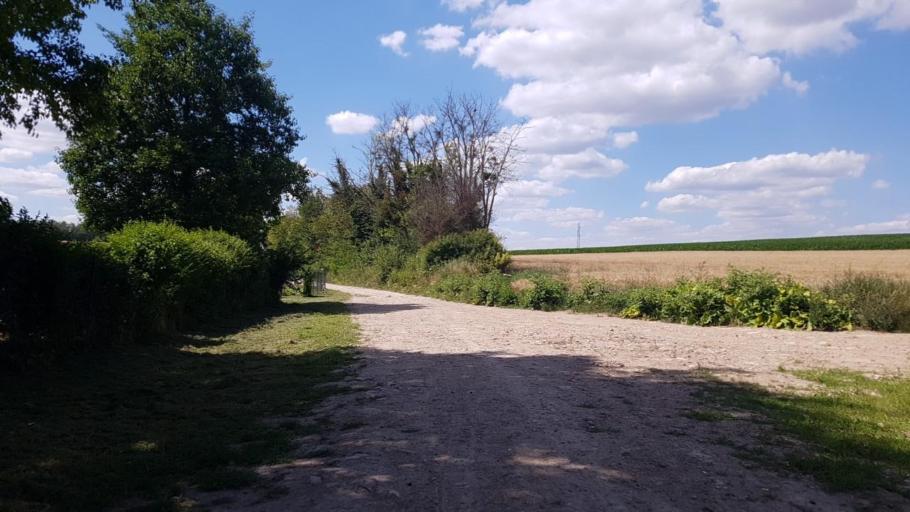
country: FR
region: Ile-de-France
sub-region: Departement de Seine-et-Marne
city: Moussy-le-Vieux
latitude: 49.0547
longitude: 2.6231
